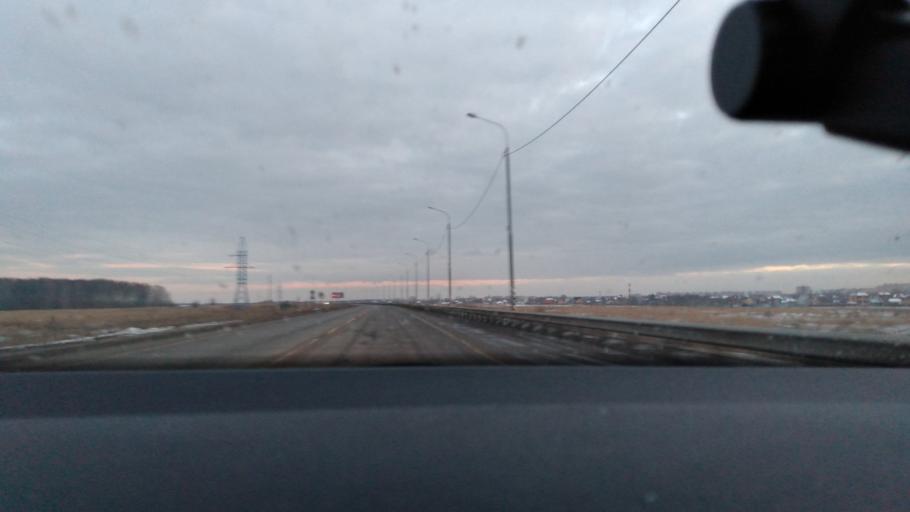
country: RU
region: Moskovskaya
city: Yegor'yevsk
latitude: 55.4023
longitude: 39.0585
